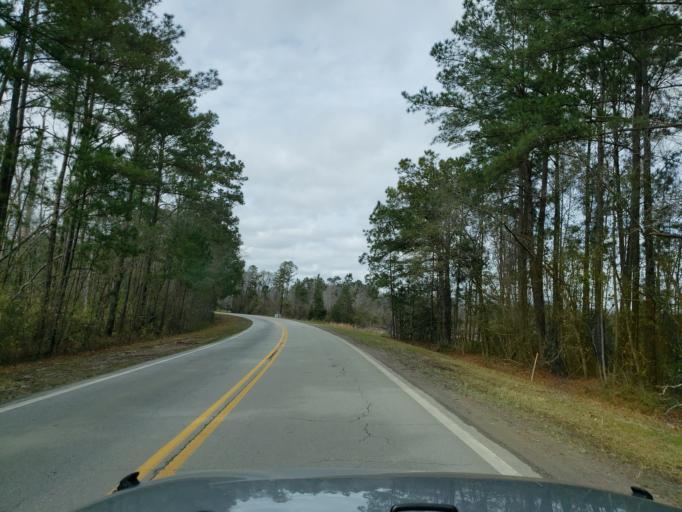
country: US
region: Georgia
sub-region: Chatham County
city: Georgetown
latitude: 32.0361
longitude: -81.2732
